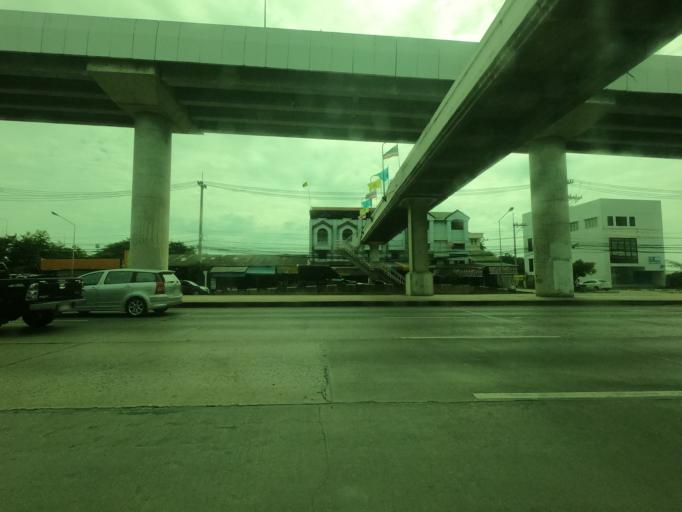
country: TH
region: Nakhon Pathom
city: Nakhon Chai Si
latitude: 13.7934
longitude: 100.1694
